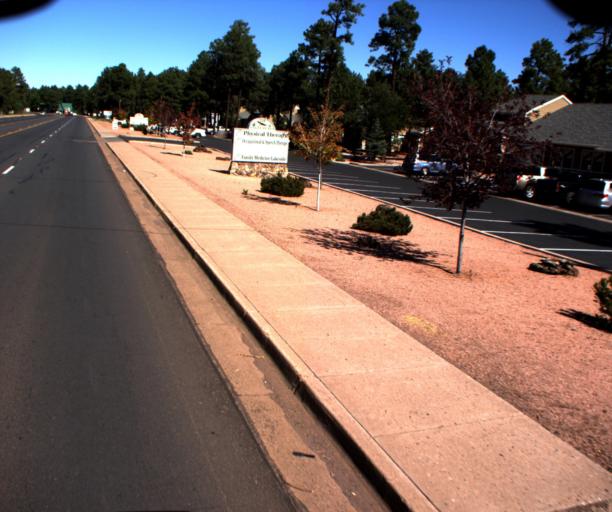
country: US
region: Arizona
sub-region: Navajo County
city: Pinetop-Lakeside
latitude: 34.1445
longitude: -109.9574
